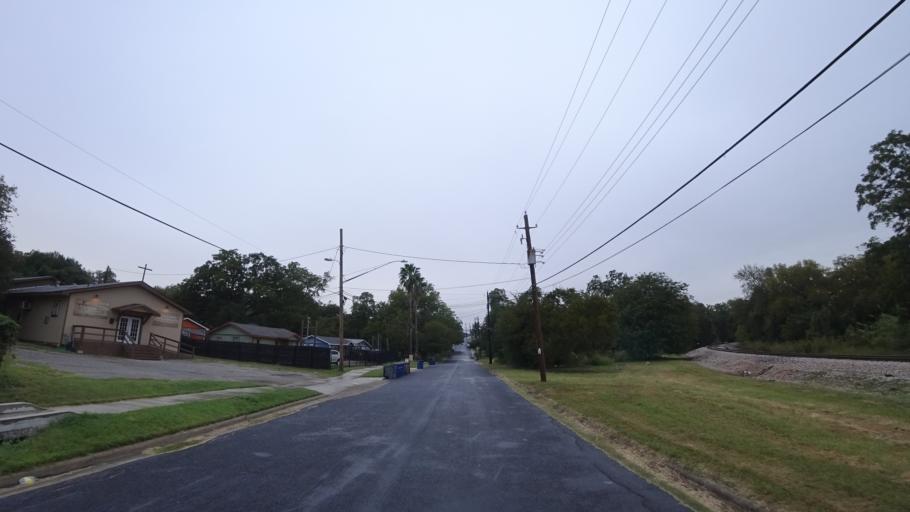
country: US
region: Texas
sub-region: Travis County
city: Austin
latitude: 30.2679
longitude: -97.7155
